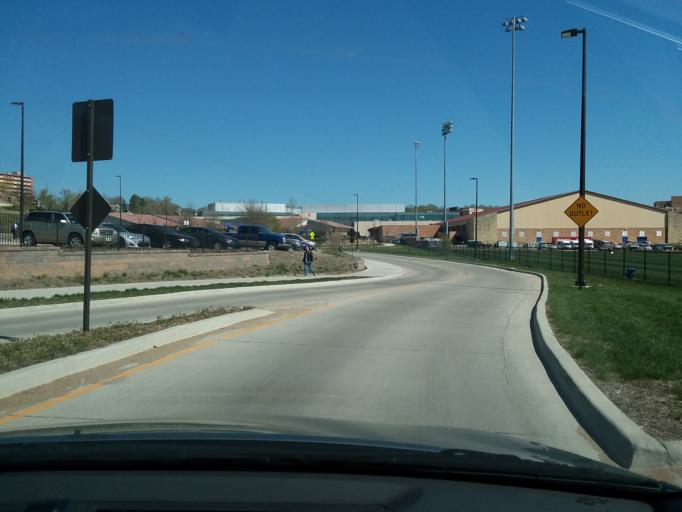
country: US
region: Kansas
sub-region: Douglas County
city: Lawrence
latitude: 38.9517
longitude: -95.2555
